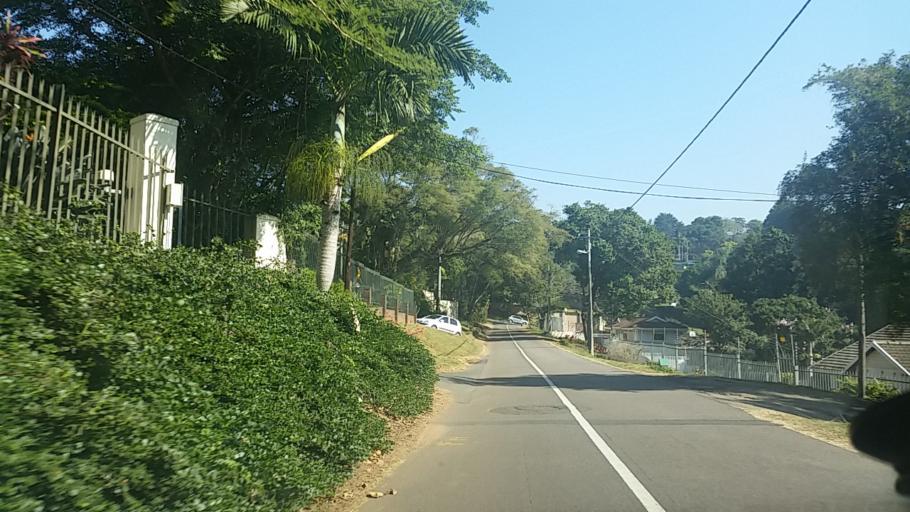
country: ZA
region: KwaZulu-Natal
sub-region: eThekwini Metropolitan Municipality
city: Berea
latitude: -29.8389
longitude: 30.9089
